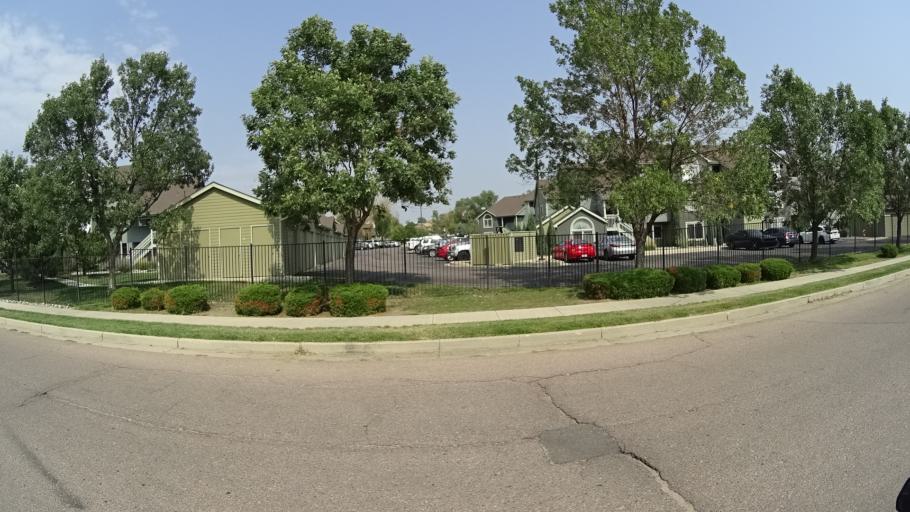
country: US
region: Colorado
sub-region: El Paso County
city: Colorado Springs
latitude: 38.8278
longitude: -104.7858
